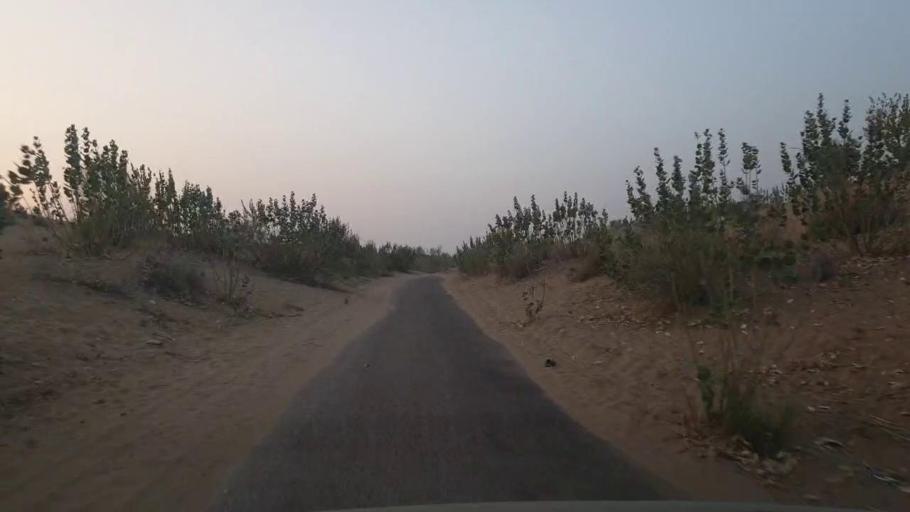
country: PK
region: Sindh
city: Umarkot
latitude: 25.3119
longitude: 70.0612
